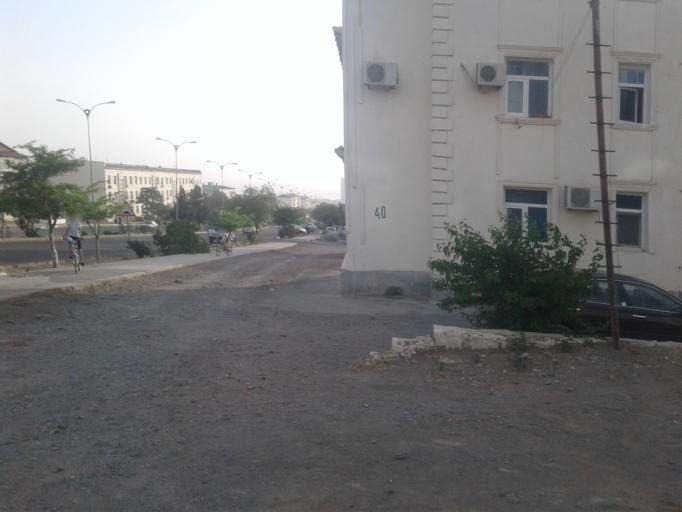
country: TM
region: Balkan
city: Turkmenbasy
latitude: 40.0018
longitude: 52.9767
